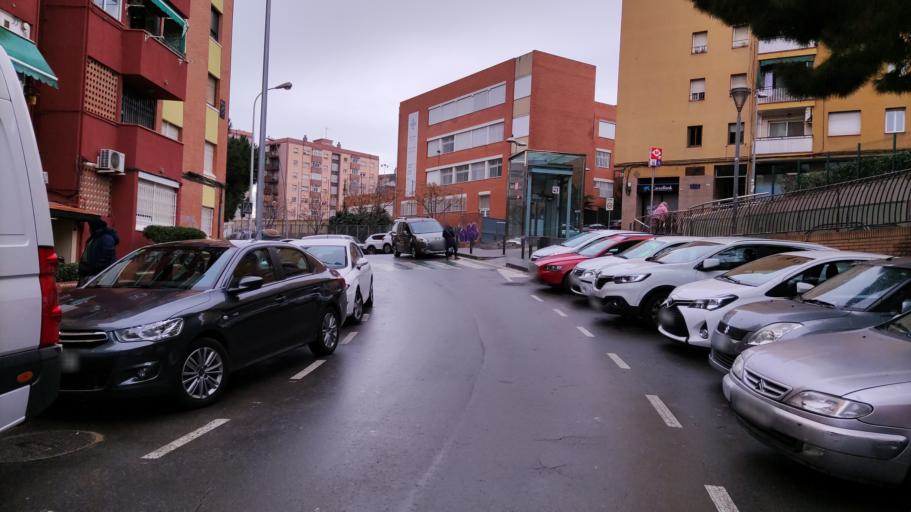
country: ES
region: Catalonia
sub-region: Provincia de Barcelona
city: Llefia
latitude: 41.4423
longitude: 2.2173
